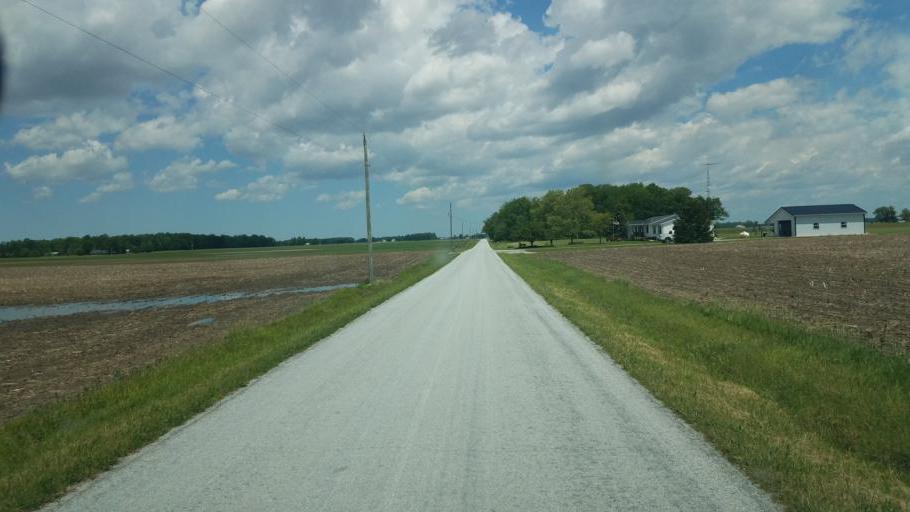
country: US
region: Ohio
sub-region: Hardin County
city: Kenton
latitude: 40.6659
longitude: -83.4771
